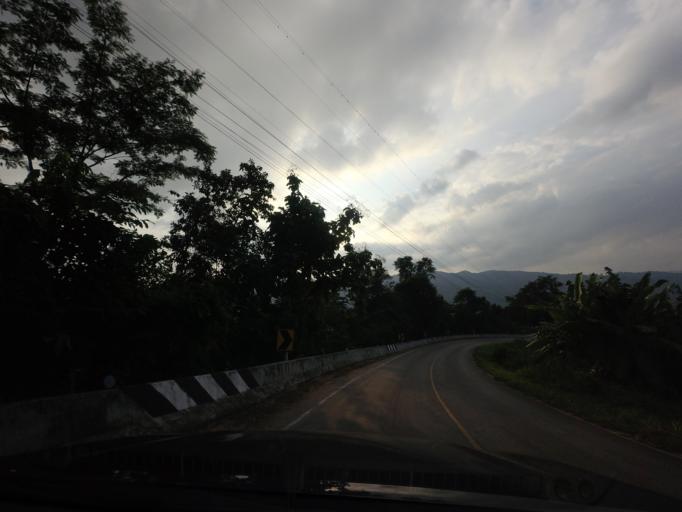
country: TH
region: Loei
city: Na Haeo
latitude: 17.3635
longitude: 101.0506
